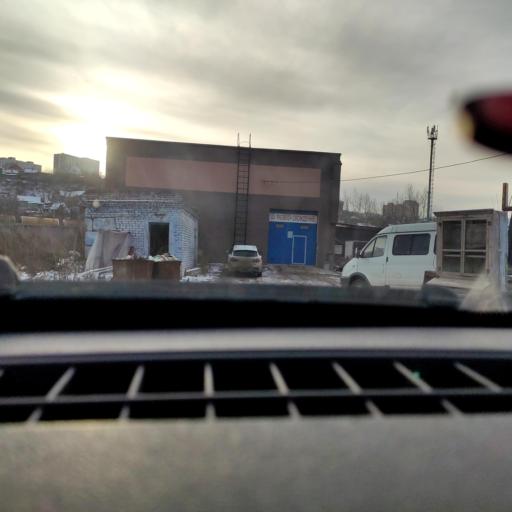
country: RU
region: Bashkortostan
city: Ufa
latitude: 54.7414
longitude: 55.9269
